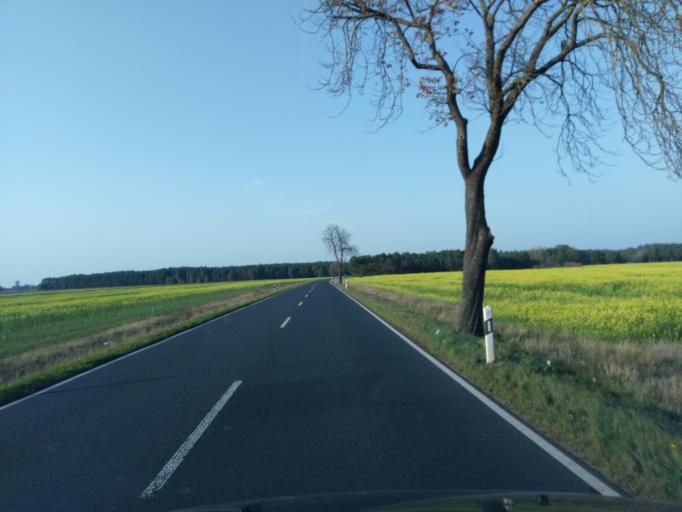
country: DE
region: Brandenburg
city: Herzberg
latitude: 51.7138
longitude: 13.2341
